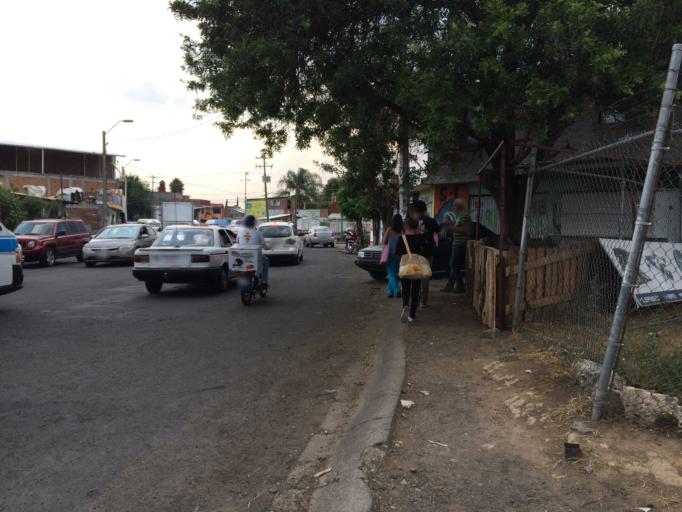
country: MX
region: Michoacan
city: Morelia
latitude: 19.6916
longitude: -101.2251
